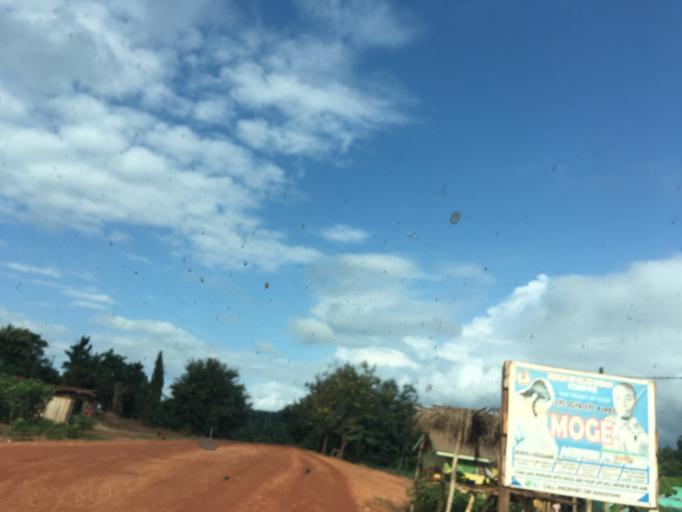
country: GH
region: Western
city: Wassa-Akropong
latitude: 5.9541
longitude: -2.4382
